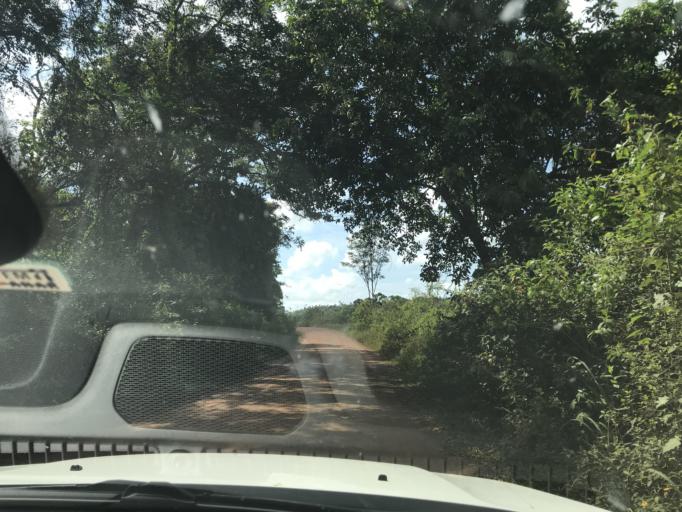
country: BR
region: Bahia
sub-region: Entre Rios
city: Entre Rios
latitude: -12.1640
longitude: -38.0750
